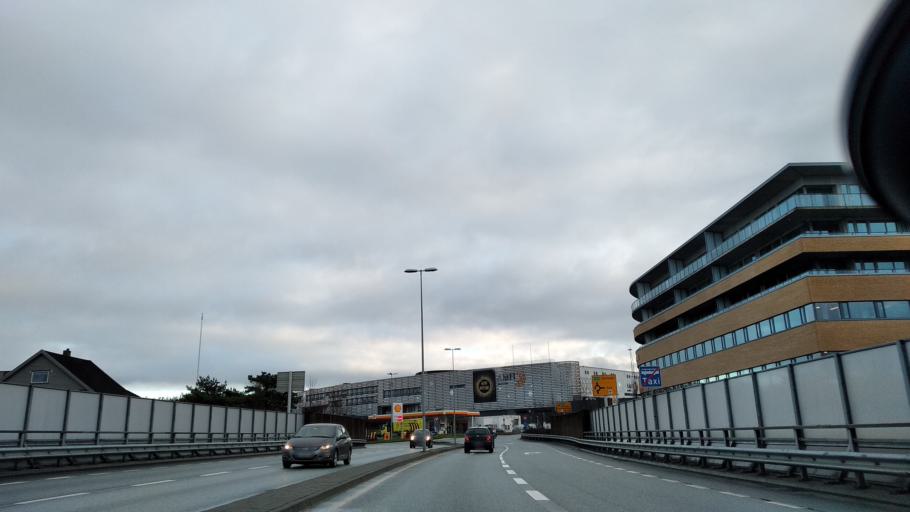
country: NO
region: Rogaland
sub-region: Stavanger
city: Stavanger
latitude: 58.9529
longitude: 5.6735
